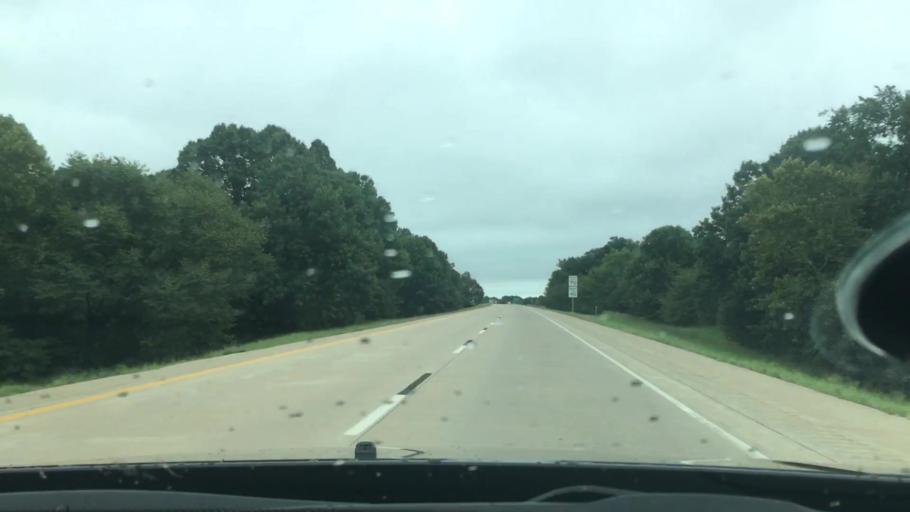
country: US
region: Oklahoma
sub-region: McIntosh County
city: Checotah
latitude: 35.4518
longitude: -95.7056
